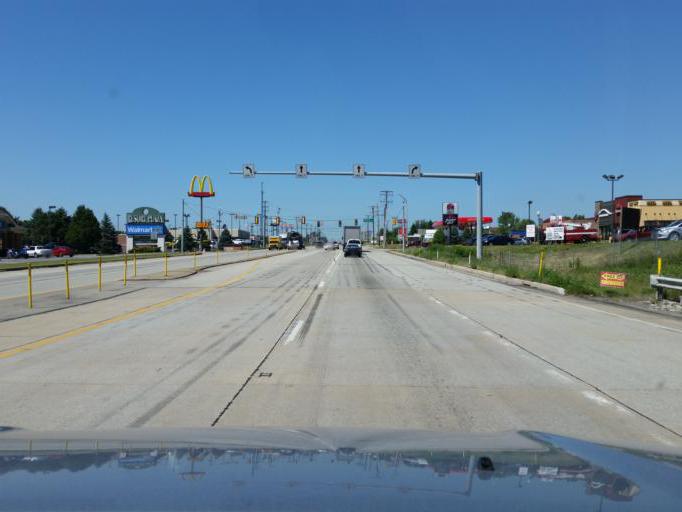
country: US
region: Pennsylvania
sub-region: Indiana County
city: Blairsville
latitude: 40.4442
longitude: -79.2276
